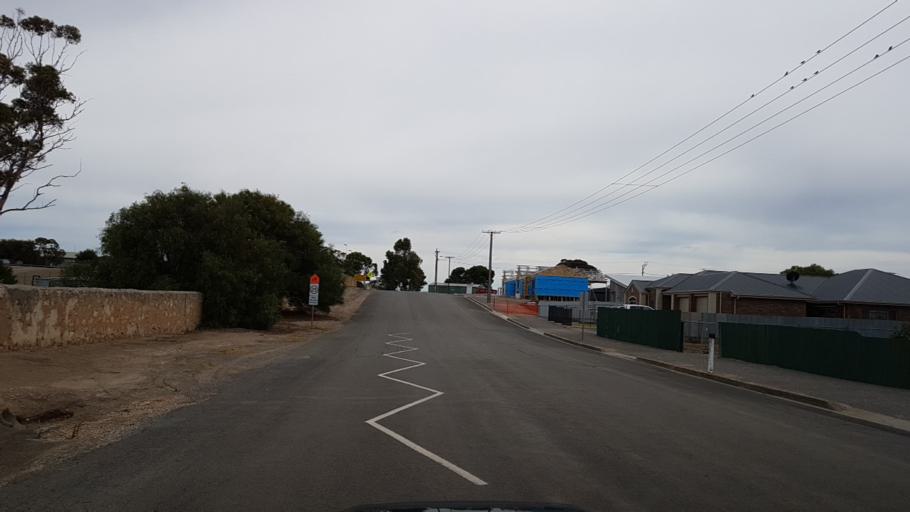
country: AU
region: South Australia
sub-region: Yorke Peninsula
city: Port Victoria
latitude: -34.7683
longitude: 137.5935
